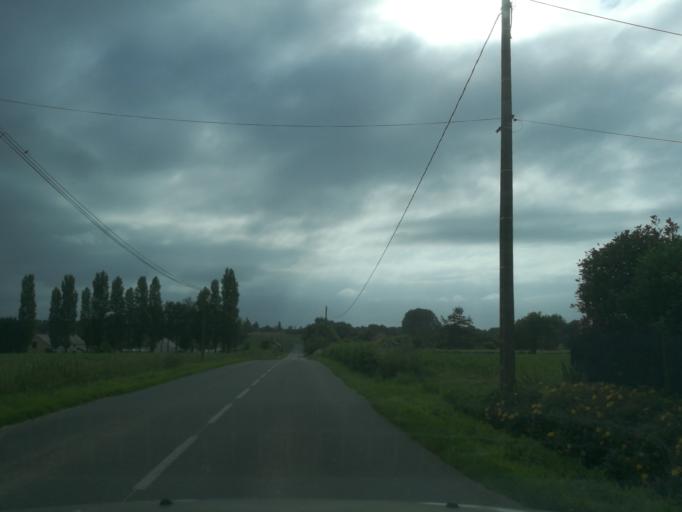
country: FR
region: Brittany
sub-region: Departement d'Ille-et-Vilaine
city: Bedee
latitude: 48.2078
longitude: -1.9455
